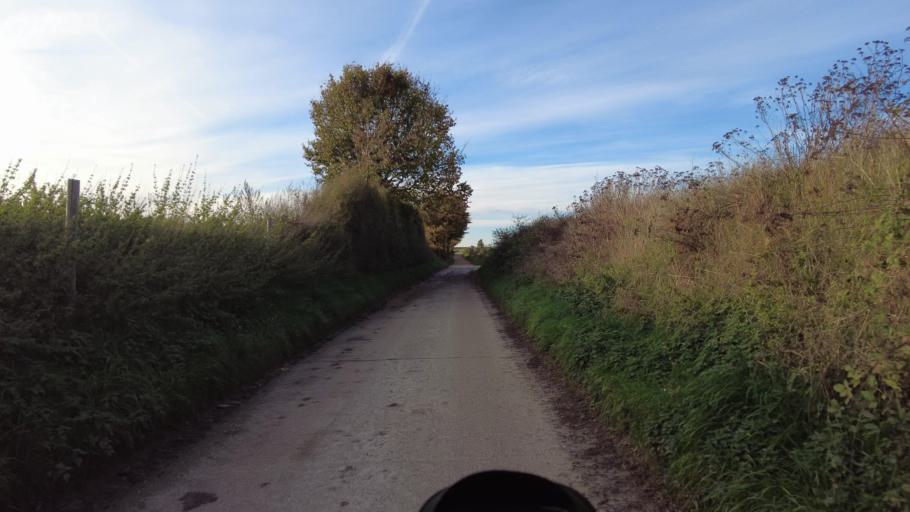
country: BE
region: Flanders
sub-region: Provincie Vlaams-Brabant
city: Hoegaarden
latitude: 50.7513
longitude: 4.9389
